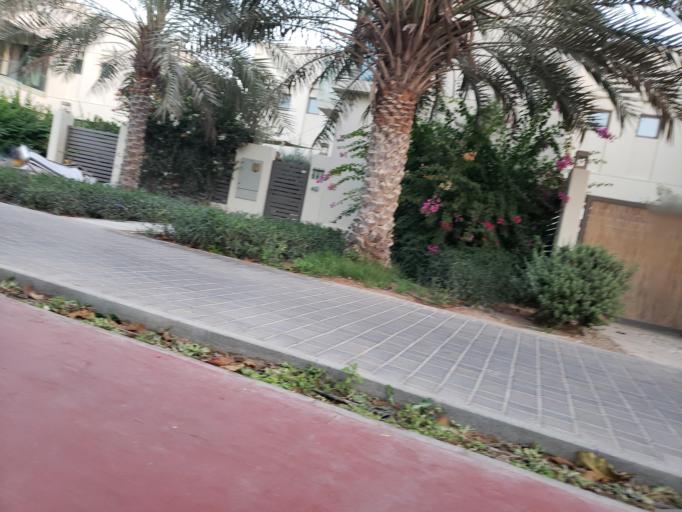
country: AE
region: Dubai
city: Dubai
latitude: 25.0302
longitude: 55.2794
